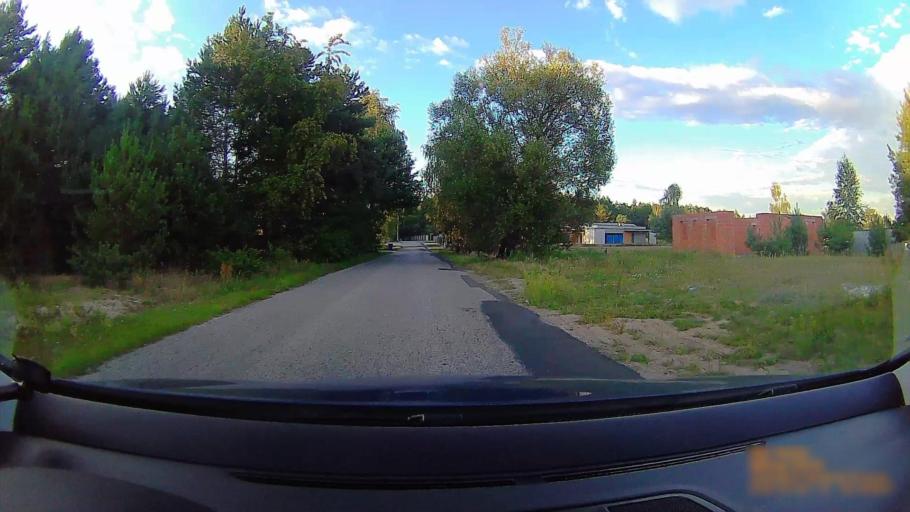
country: PL
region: Greater Poland Voivodeship
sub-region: Konin
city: Konin
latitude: 52.2022
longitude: 18.3219
